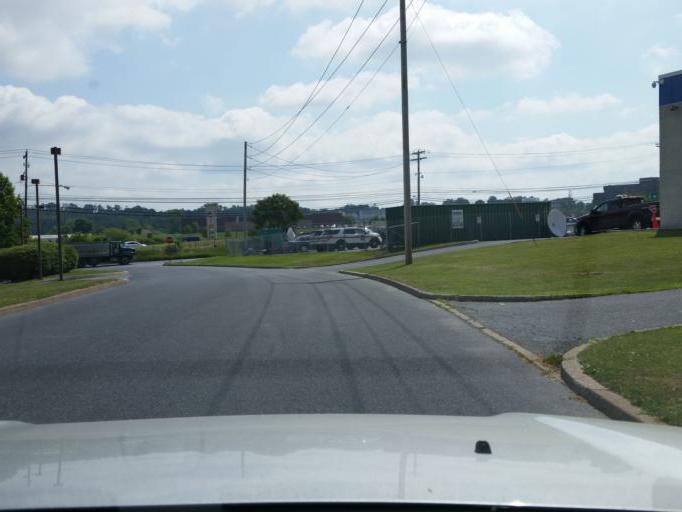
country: US
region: Pennsylvania
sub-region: Dauphin County
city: Lawnton
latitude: 40.2458
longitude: -76.8115
